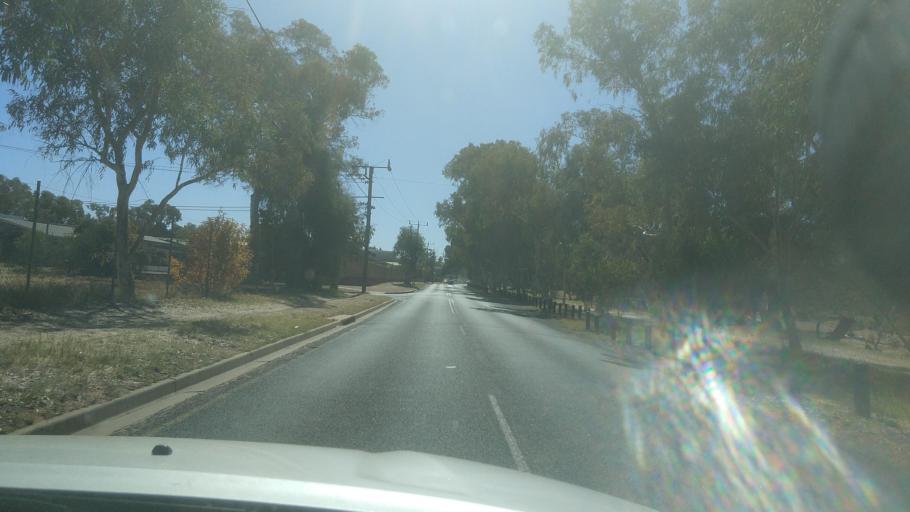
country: AU
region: Northern Territory
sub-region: Alice Springs
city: Alice Springs
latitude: -23.7106
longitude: 133.8781
